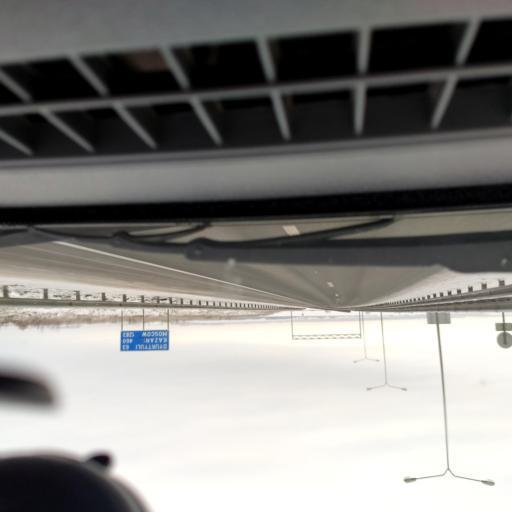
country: RU
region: Bashkortostan
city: Kushnarenkovo
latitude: 55.0643
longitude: 55.3139
